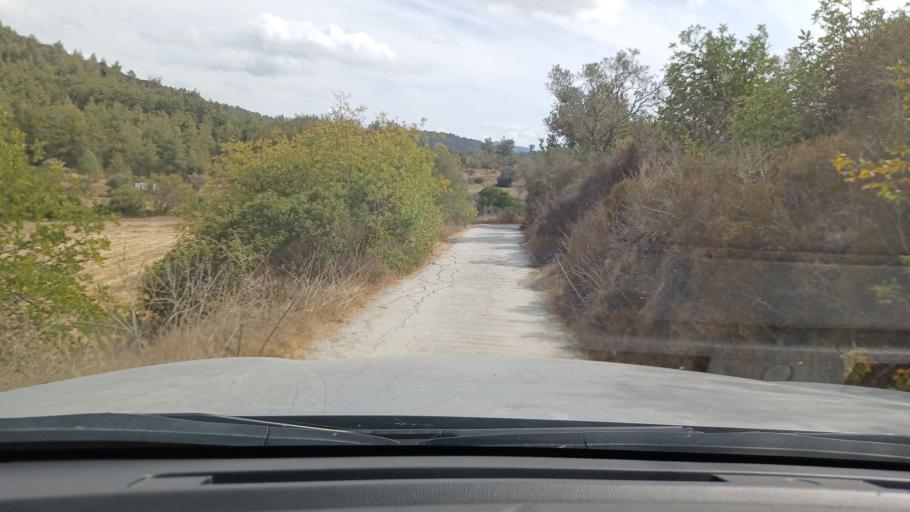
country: CY
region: Pafos
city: Polis
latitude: 35.0005
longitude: 32.5268
